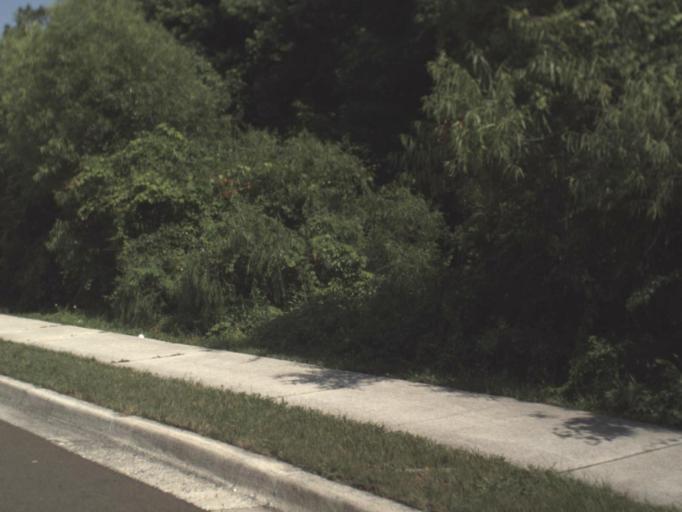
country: US
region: Florida
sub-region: Duval County
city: Atlantic Beach
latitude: 30.3602
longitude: -81.4988
